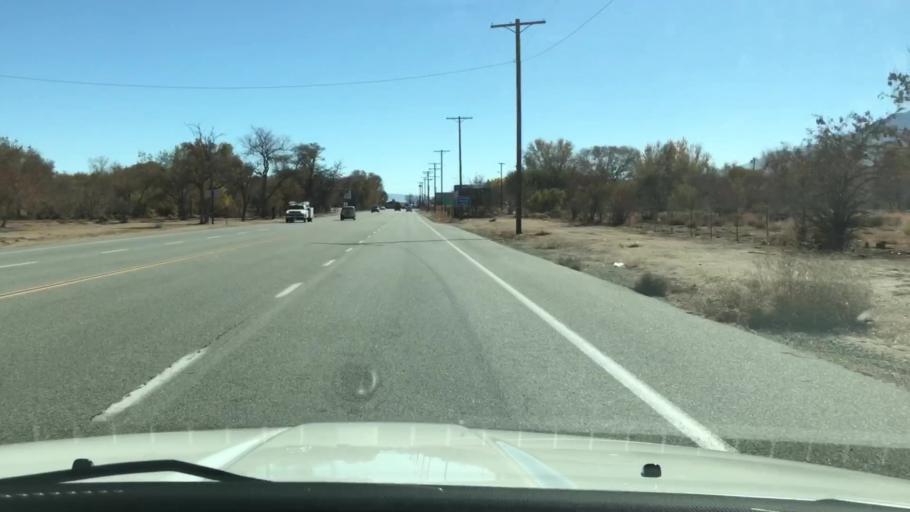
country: US
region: California
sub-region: Inyo County
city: Lone Pine
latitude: 36.5984
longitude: -118.0599
